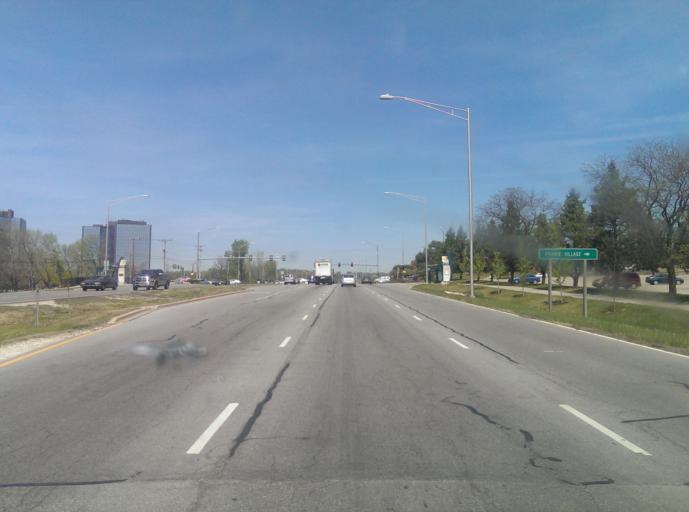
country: US
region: Kansas
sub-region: Johnson County
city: Overland Park
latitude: 38.9552
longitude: -94.6675
